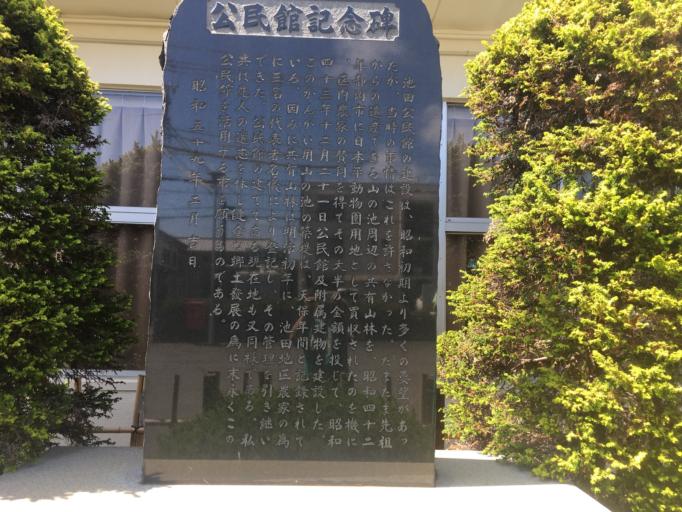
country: JP
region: Shizuoka
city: Shizuoka-shi
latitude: 34.9807
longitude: 138.4282
